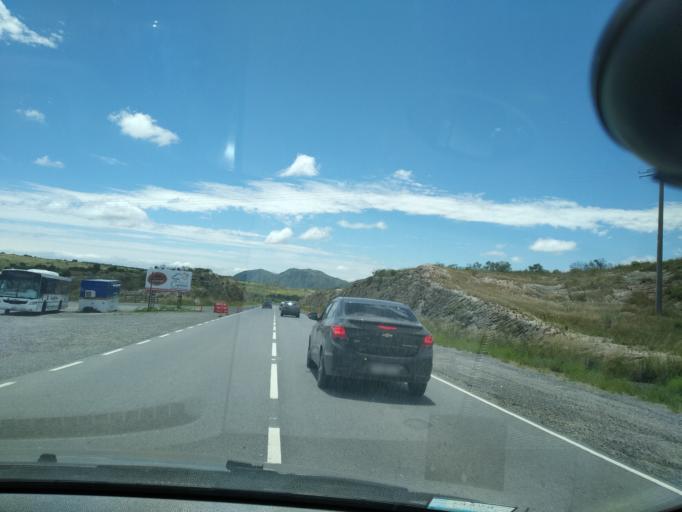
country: AR
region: Cordoba
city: Cuesta Blanca
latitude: -31.5797
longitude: -64.6067
